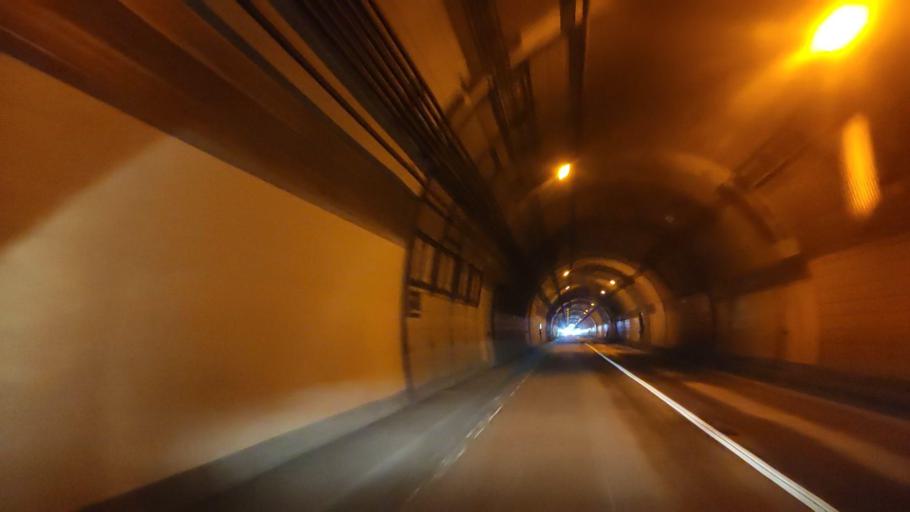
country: JP
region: Hokkaido
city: Rumoi
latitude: 43.8048
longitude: 141.3893
